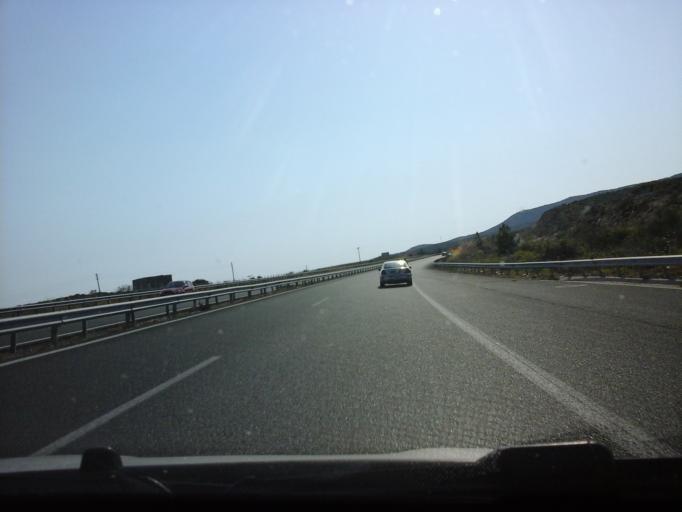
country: GR
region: East Macedonia and Thrace
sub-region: Nomos Evrou
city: Alexandroupoli
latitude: 40.8679
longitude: 25.7788
